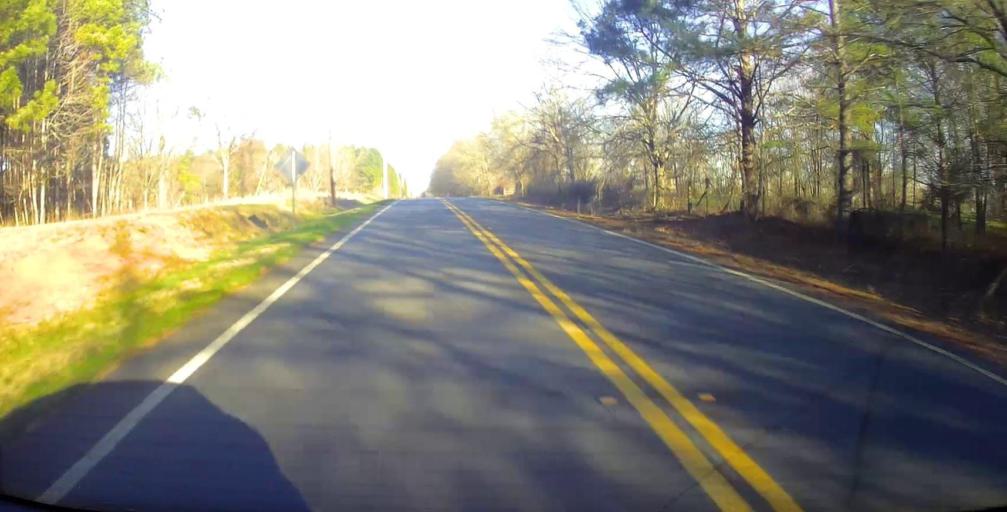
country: US
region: Georgia
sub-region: Harris County
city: Pine Mountain
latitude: 32.9162
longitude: -84.7928
